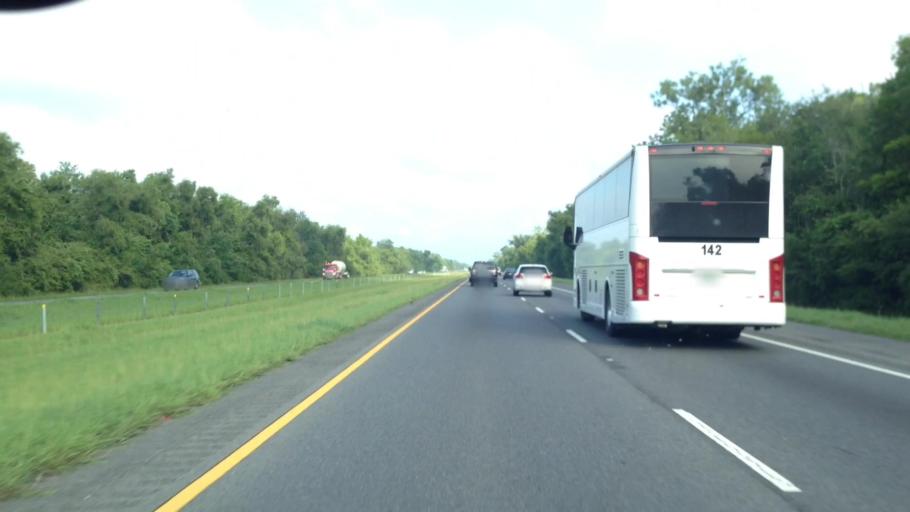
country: US
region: Louisiana
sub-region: Saint James Parish
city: Grand Point
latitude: 30.1368
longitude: -90.7365
